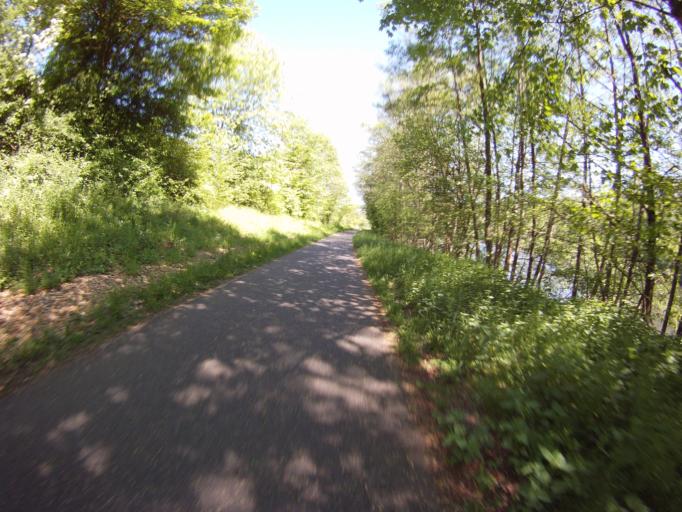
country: FR
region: Lorraine
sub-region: Departement de Meurthe-et-Moselle
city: Chaligny
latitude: 48.6399
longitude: 6.0398
